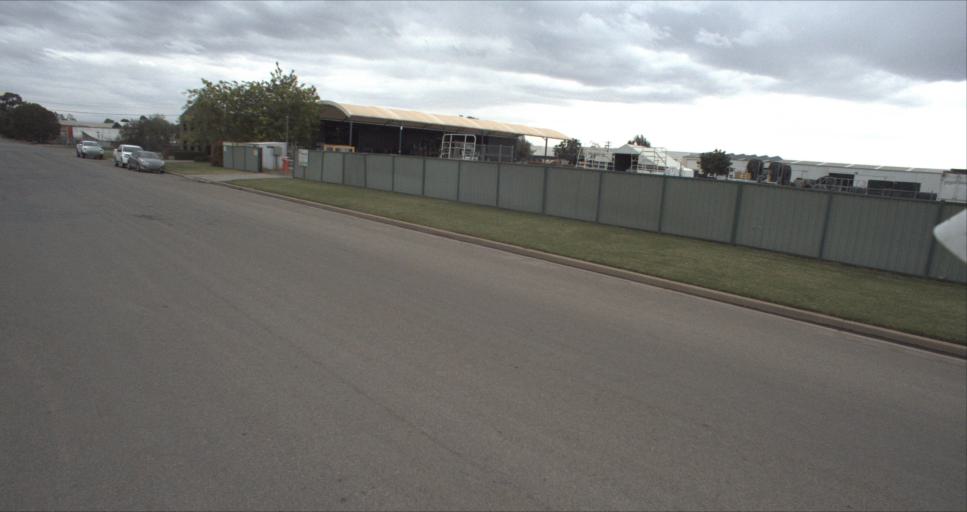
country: AU
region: New South Wales
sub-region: Leeton
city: Leeton
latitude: -34.5477
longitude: 146.3908
